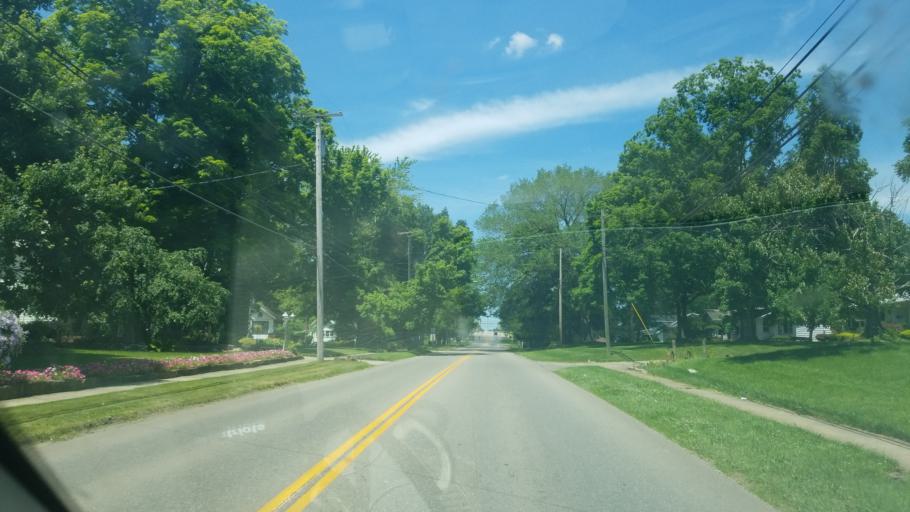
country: US
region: Ohio
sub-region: Columbiana County
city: Lisbon
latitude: 40.7816
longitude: -80.7713
